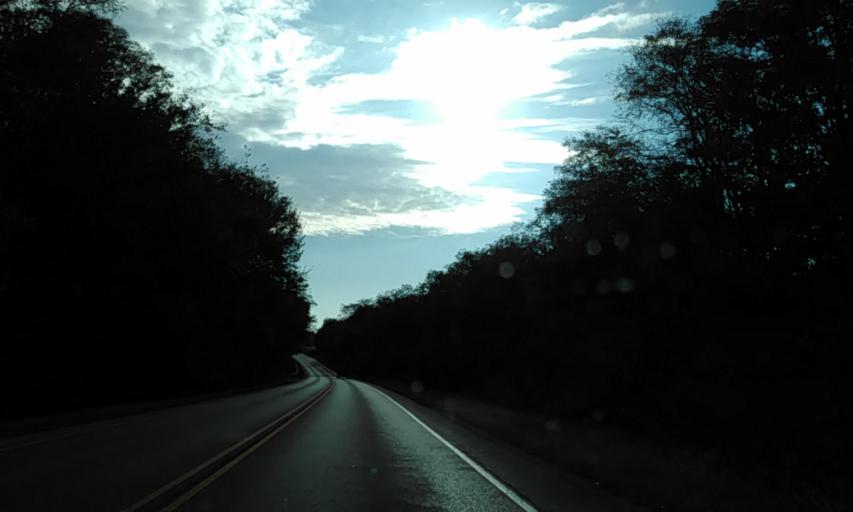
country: US
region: Illinois
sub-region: Madison County
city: Highland
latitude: 38.7720
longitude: -89.6460
